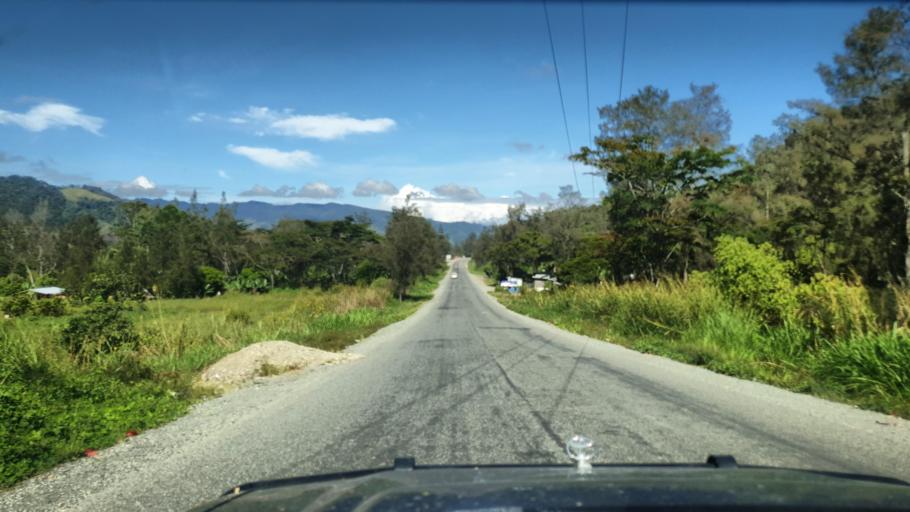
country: PG
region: Western Highlands
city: Rauna
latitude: -5.8292
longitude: 144.3704
